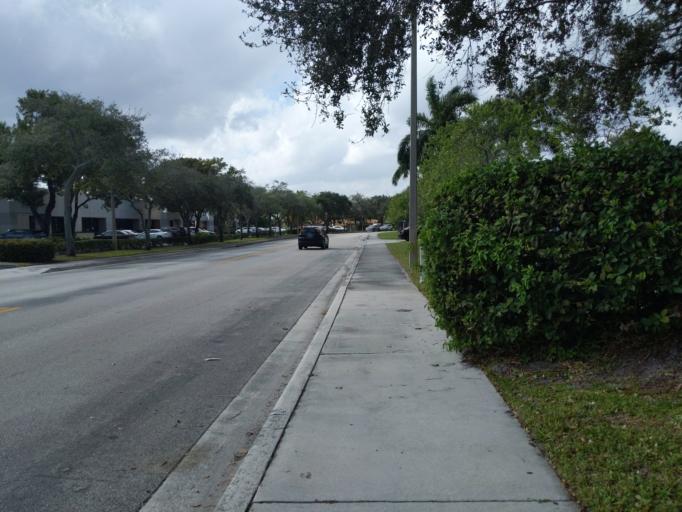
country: US
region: Florida
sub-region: Palm Beach County
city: Mangonia Park
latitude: 26.7573
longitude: -80.0941
